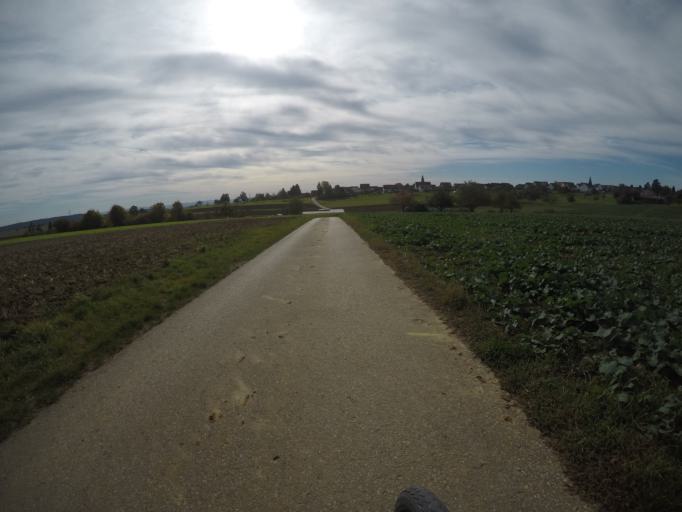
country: DE
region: Baden-Wuerttemberg
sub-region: Regierungsbezirk Stuttgart
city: Deckenpfronn
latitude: 48.6295
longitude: 8.8373
